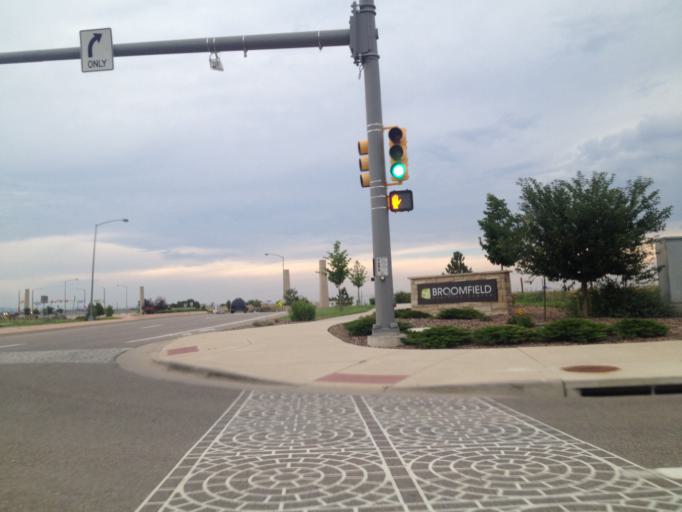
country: US
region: Colorado
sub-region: Boulder County
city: Louisville
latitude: 39.9465
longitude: -105.1232
